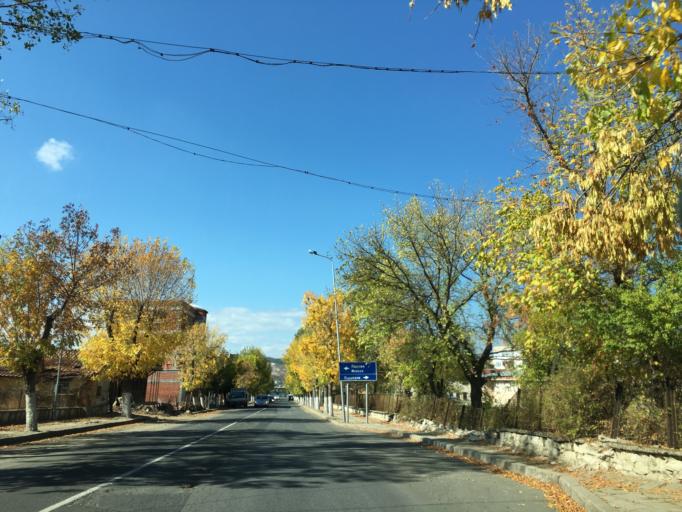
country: BG
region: Kurdzhali
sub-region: Obshtina Dzhebel
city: Dzhebel
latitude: 41.5199
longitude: 25.4151
